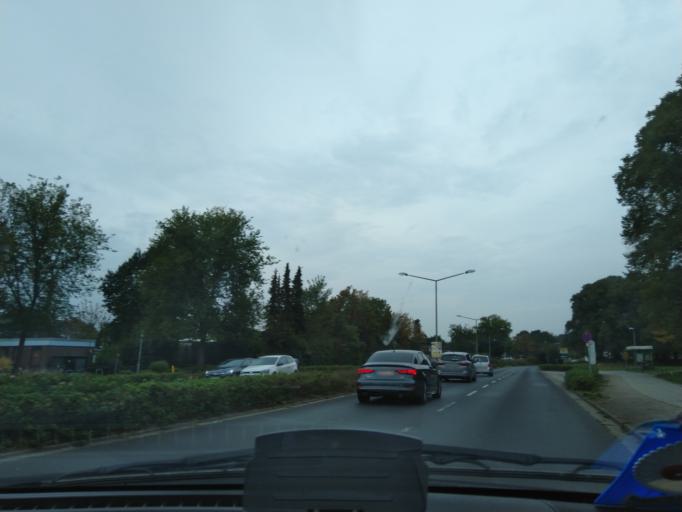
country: DE
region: Lower Saxony
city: Meppen
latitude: 52.6905
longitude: 7.2871
